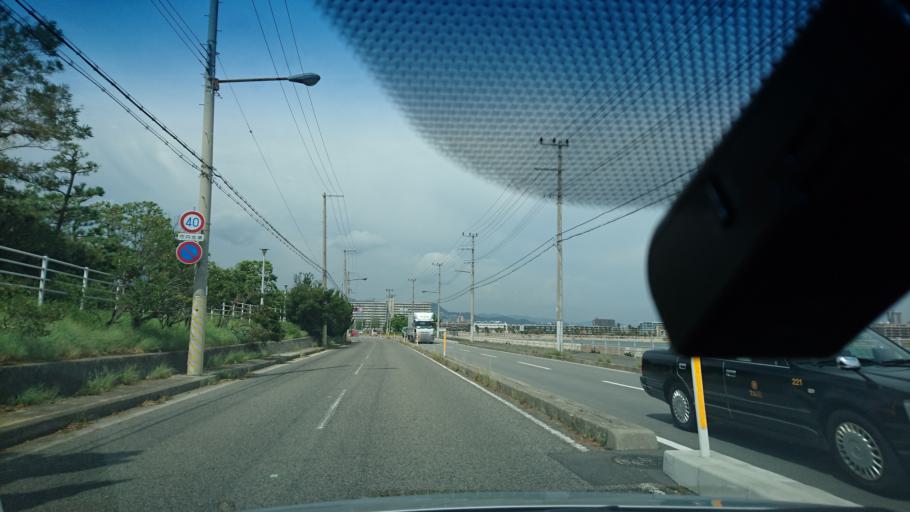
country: JP
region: Hyogo
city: Nishinomiya-hama
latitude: 34.7205
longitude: 135.3237
